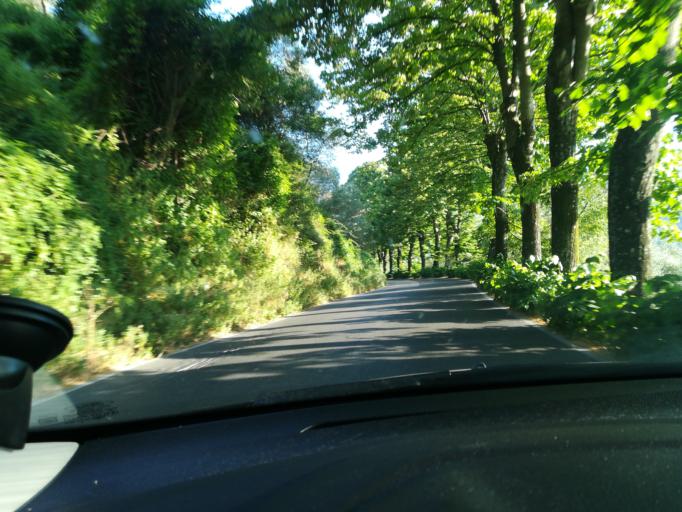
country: IT
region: Tuscany
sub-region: Provincia di Lucca
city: Stiava
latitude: 43.9133
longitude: 10.3394
